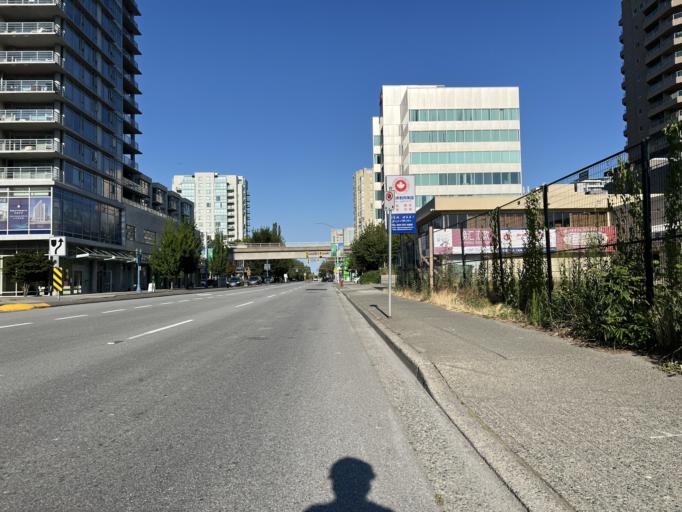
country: CA
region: British Columbia
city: Richmond
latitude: 49.1703
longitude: -123.1345
